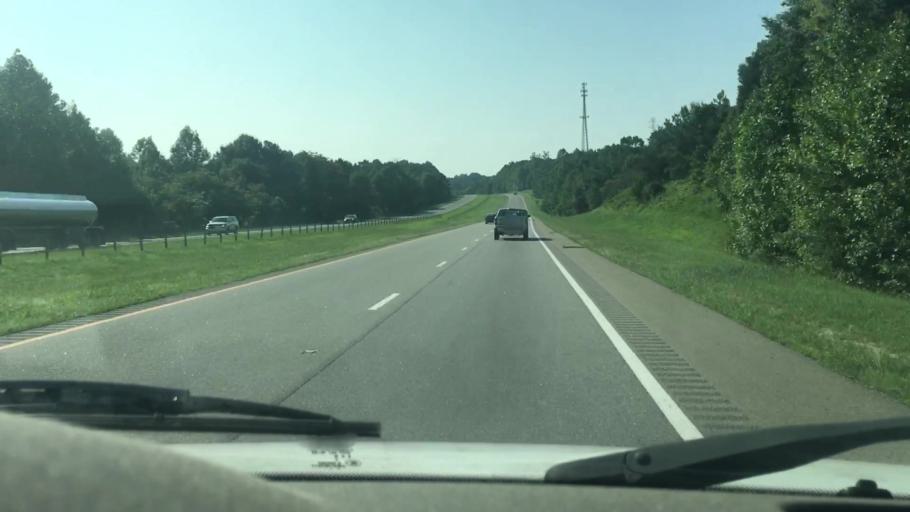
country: US
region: North Carolina
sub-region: Lincoln County
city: Lowesville
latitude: 35.3752
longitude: -80.9974
